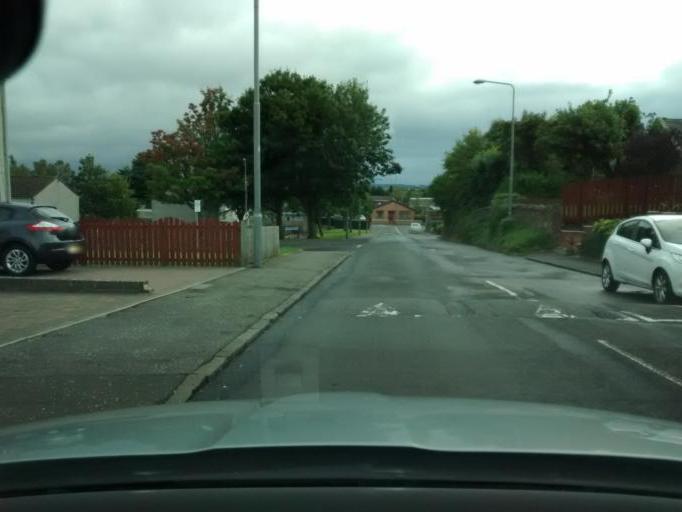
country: GB
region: Scotland
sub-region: West Lothian
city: Bathgate
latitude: 55.9020
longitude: -3.6575
